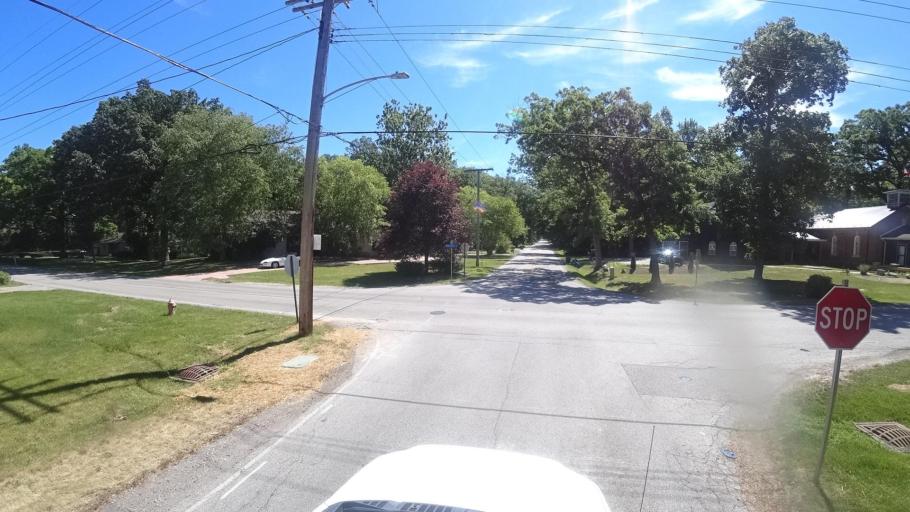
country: US
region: Indiana
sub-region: Porter County
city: Porter
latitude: 41.6296
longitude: -87.0675
